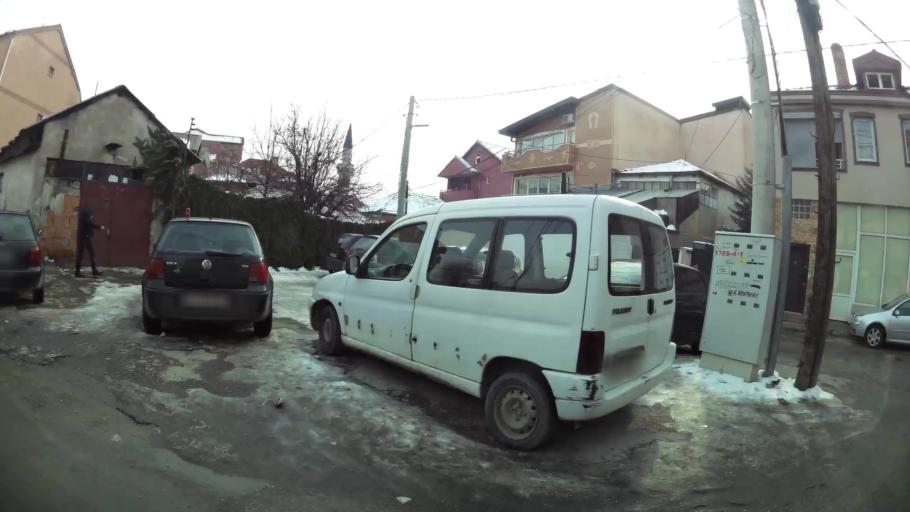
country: MK
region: Cair
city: Cair
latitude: 42.0105
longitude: 21.4369
